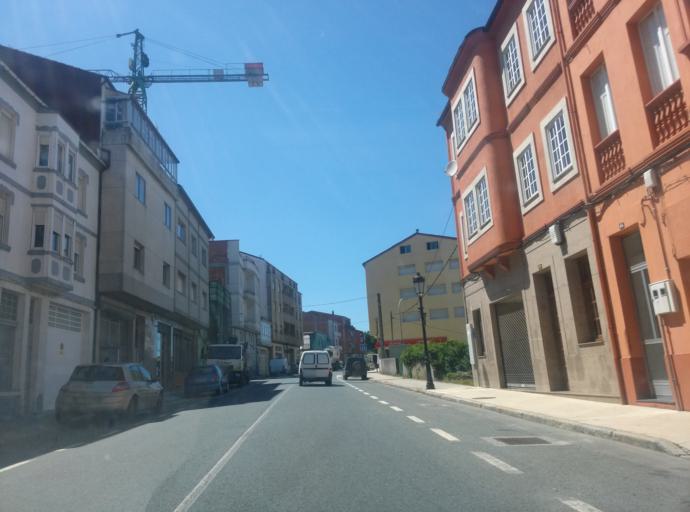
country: ES
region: Galicia
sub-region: Provincia de Lugo
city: Meira
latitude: 43.2134
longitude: -7.2965
